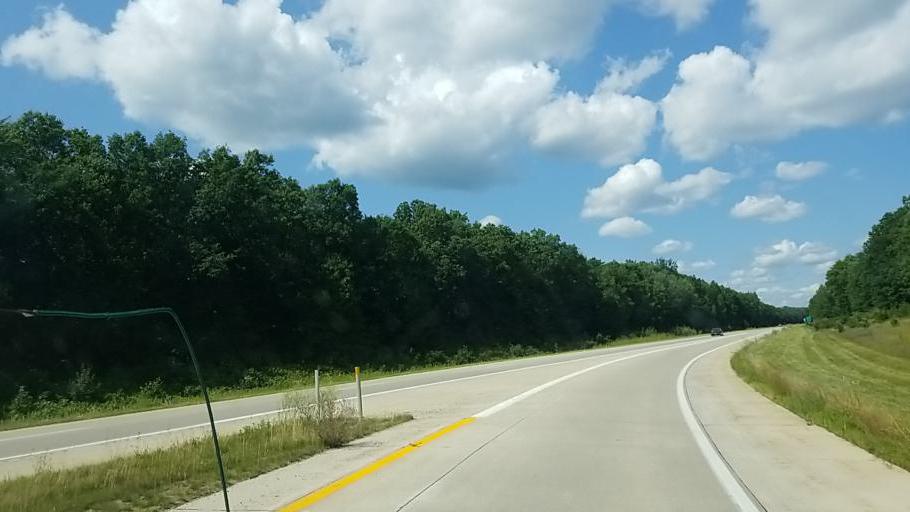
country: US
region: Michigan
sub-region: Montcalm County
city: Howard City
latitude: 43.3993
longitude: -85.5118
